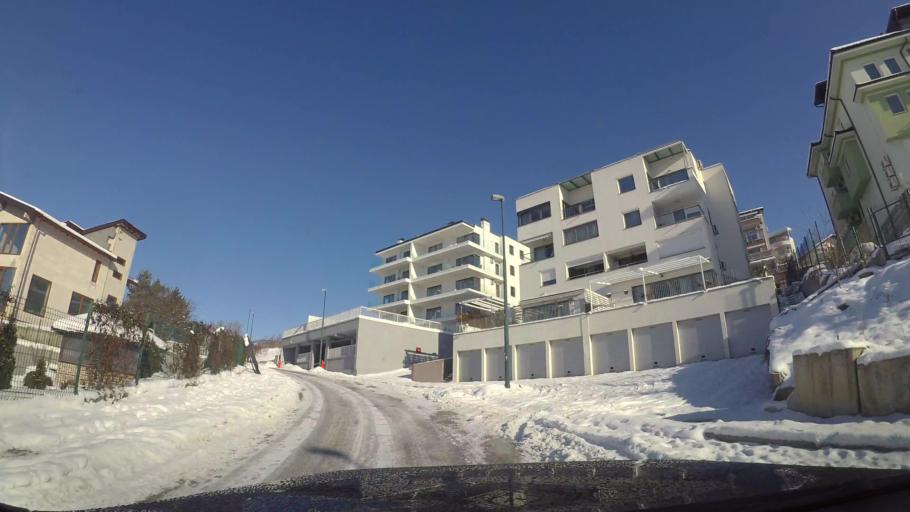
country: BA
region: Federation of Bosnia and Herzegovina
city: Kobilja Glava
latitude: 43.8806
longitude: 18.4103
